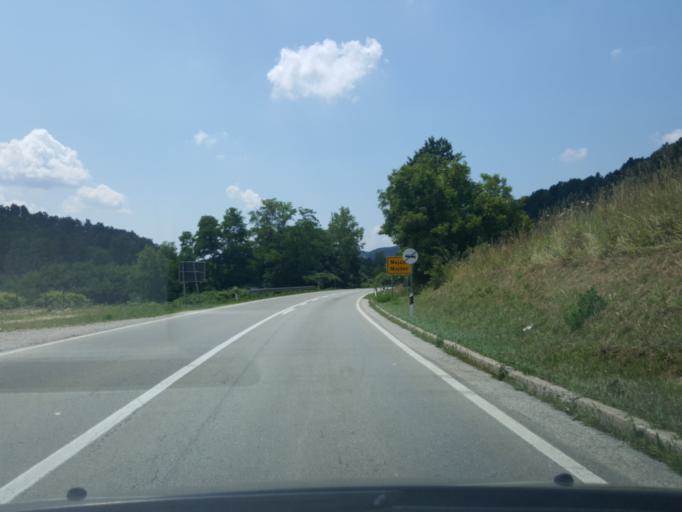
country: RS
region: Central Serbia
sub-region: Moravicki Okrug
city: Gornji Milanovac
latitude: 44.1057
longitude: 20.4833
